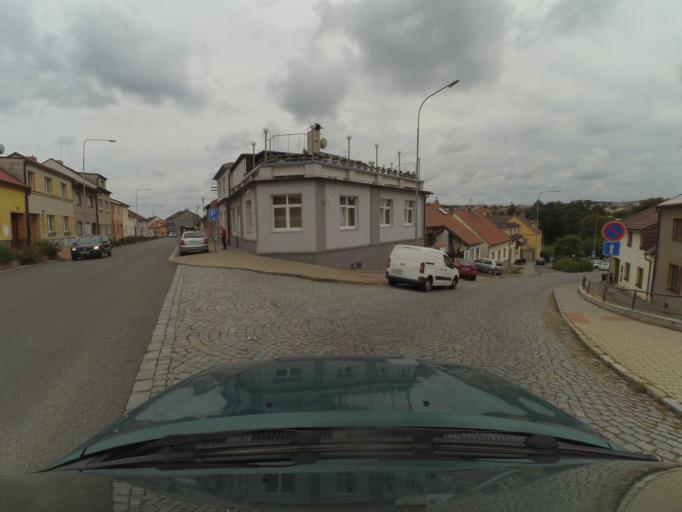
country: CZ
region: Central Bohemia
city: Rakovnik
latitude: 50.1047
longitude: 13.7358
